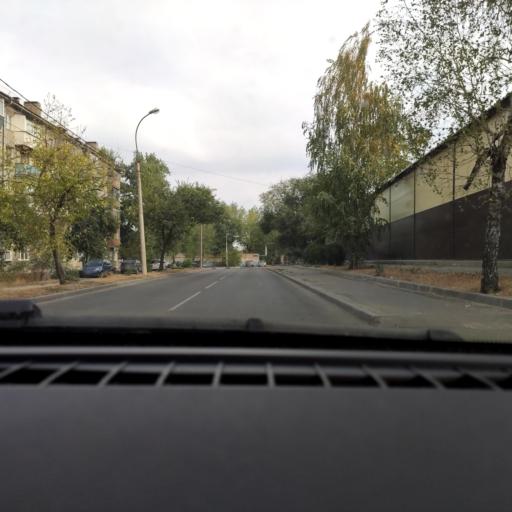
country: RU
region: Voronezj
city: Voronezh
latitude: 51.6408
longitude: 39.2459
